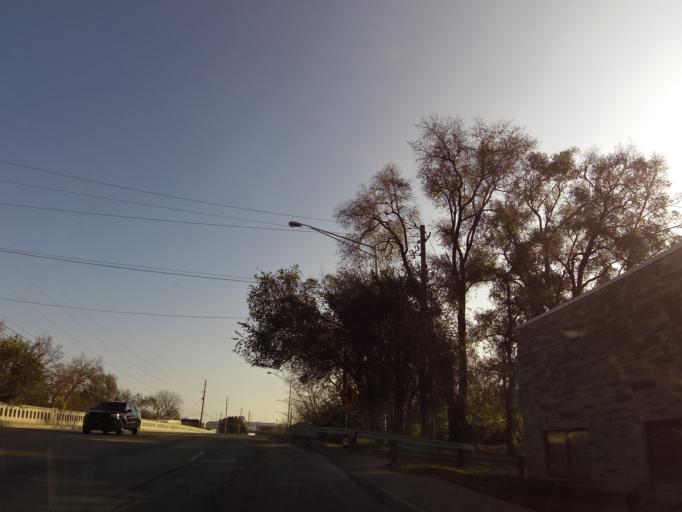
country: US
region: Indiana
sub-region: Marion County
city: Indianapolis
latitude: 39.7887
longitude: -86.1787
